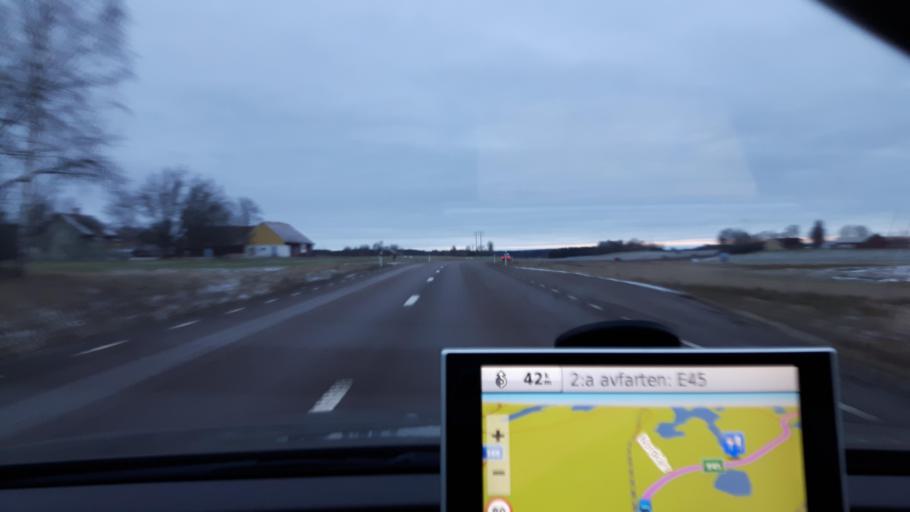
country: SE
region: Vaestra Goetaland
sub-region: Melleruds Kommun
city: Mellerud
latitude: 58.7226
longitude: 12.4550
